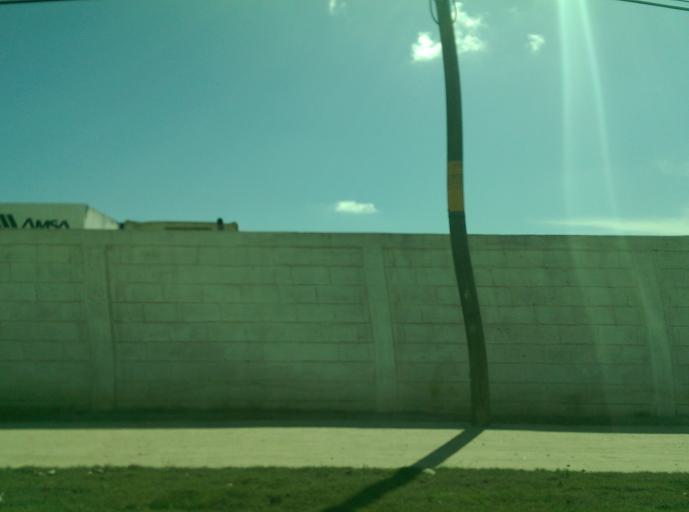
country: MX
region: Tabasco
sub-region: Centro
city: Anacleto Canabal 2da. Seccion
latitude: 17.9834
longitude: -93.0106
